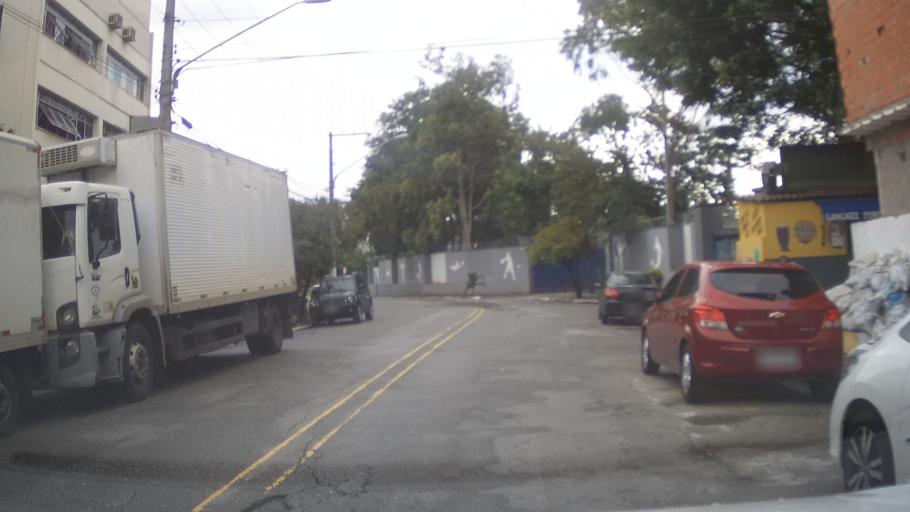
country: BR
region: Sao Paulo
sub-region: Sao Paulo
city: Sao Paulo
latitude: -23.5133
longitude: -46.6692
